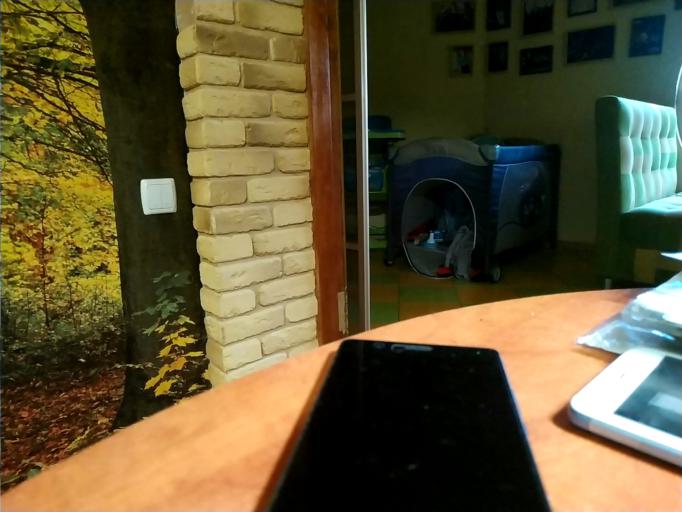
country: RU
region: Orjol
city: Znamenskoye
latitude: 53.5289
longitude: 35.4964
